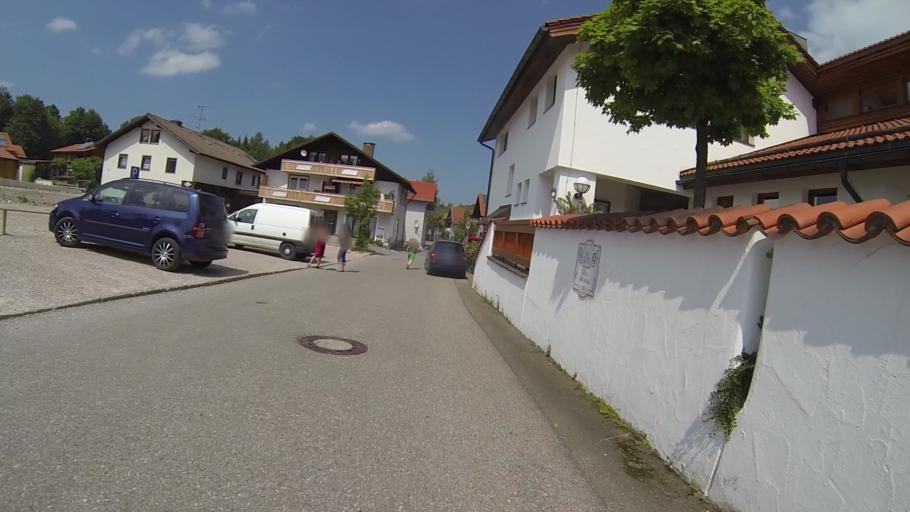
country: DE
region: Bavaria
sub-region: Swabia
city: Nesselwang
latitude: 47.6226
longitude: 10.4990
